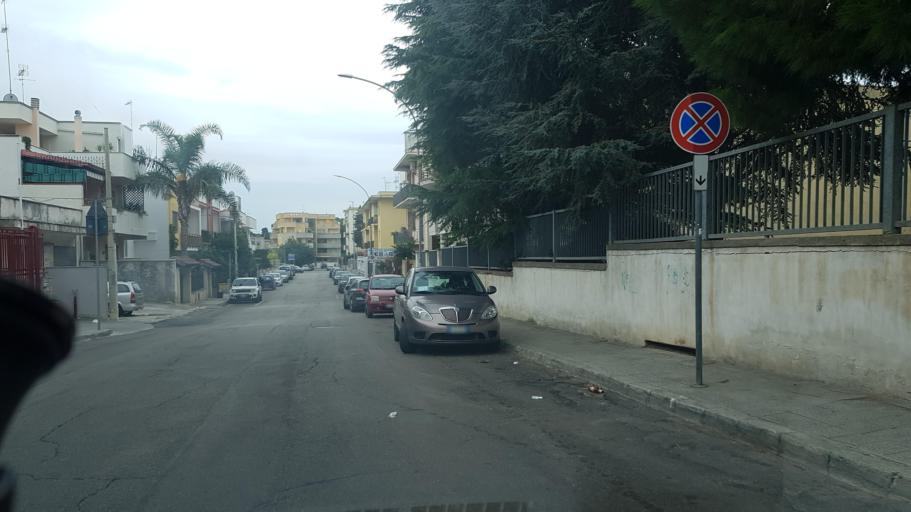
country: IT
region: Apulia
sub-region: Provincia di Lecce
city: Lecce
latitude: 40.3455
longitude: 18.1581
